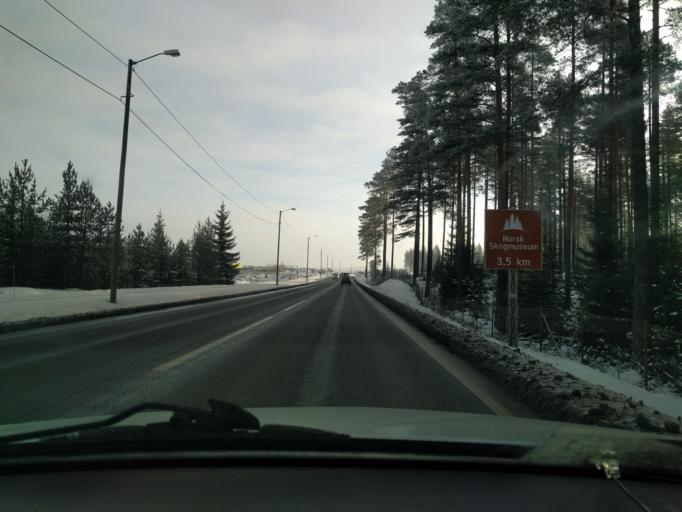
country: NO
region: Hedmark
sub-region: Elverum
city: Elverum
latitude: 60.8844
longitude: 11.5198
